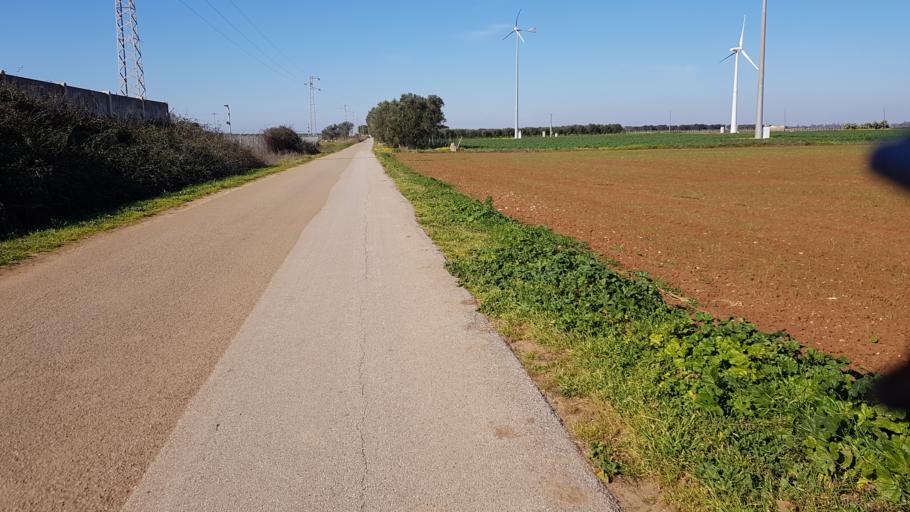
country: IT
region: Apulia
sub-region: Provincia di Brindisi
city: Brindisi
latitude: 40.6179
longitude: 17.8646
